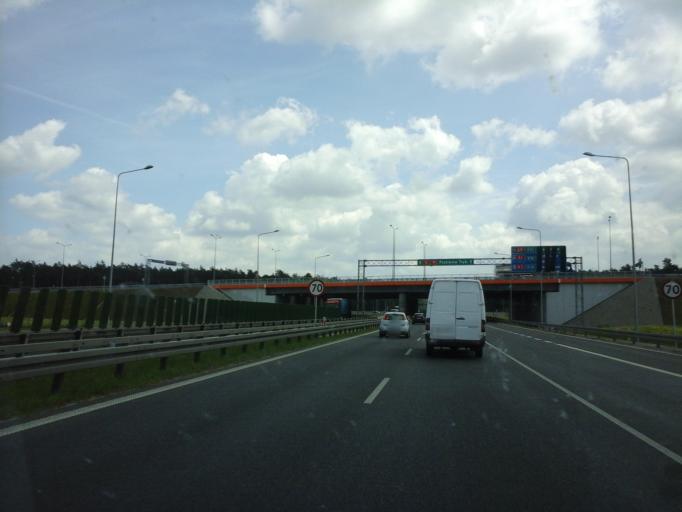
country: PL
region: Lodz Voivodeship
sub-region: Powiat lodzki wschodni
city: Rzgow
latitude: 51.6398
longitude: 19.4977
